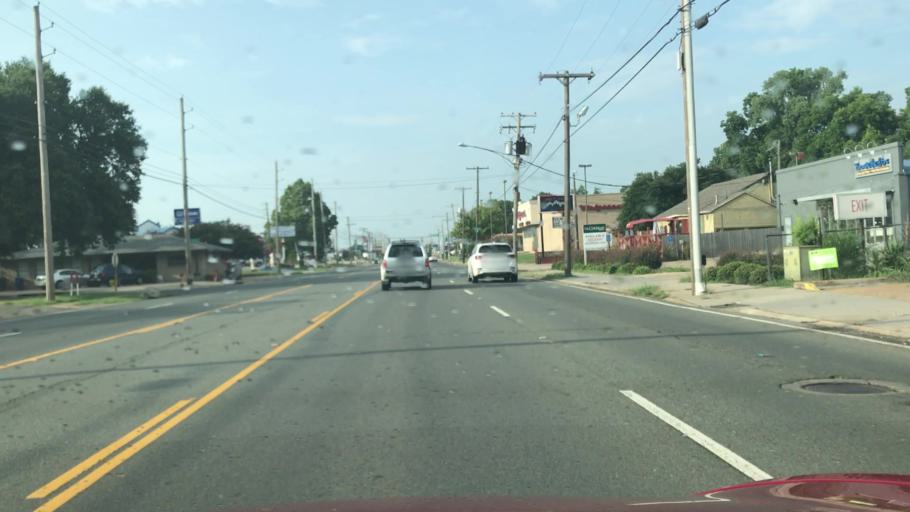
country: US
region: Louisiana
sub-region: Bossier Parish
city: Bossier City
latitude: 32.4587
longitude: -93.7222
